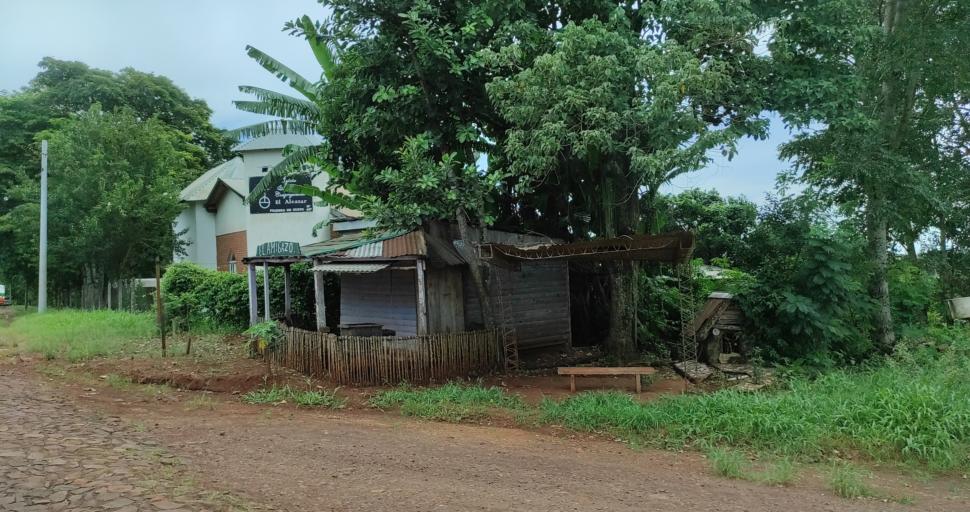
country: AR
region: Misiones
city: El Alcazar
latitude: -26.7227
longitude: -54.8102
